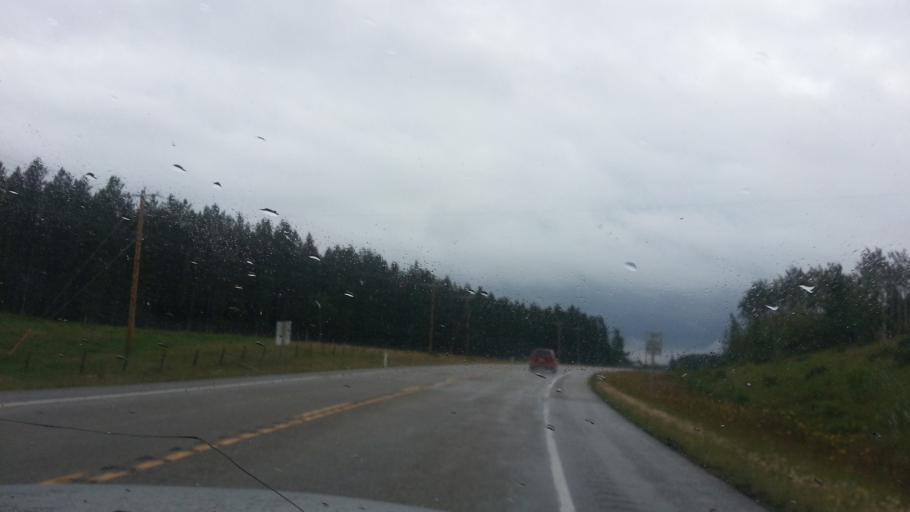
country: CA
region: Alberta
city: Cochrane
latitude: 50.9209
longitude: -114.6033
